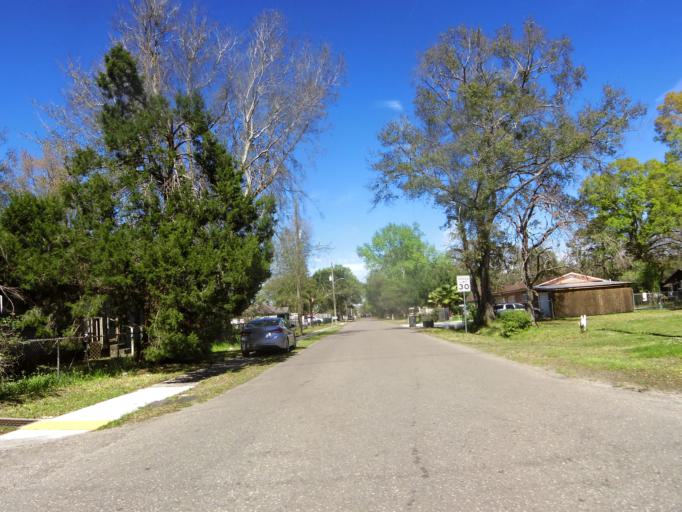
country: US
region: Florida
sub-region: Duval County
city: Jacksonville
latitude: 30.3226
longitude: -81.7174
